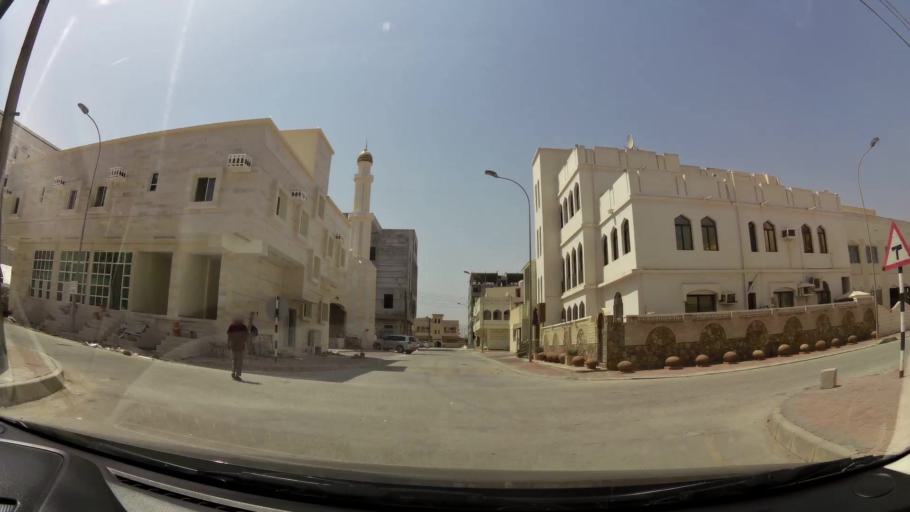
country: OM
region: Zufar
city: Salalah
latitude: 17.0202
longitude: 54.0878
